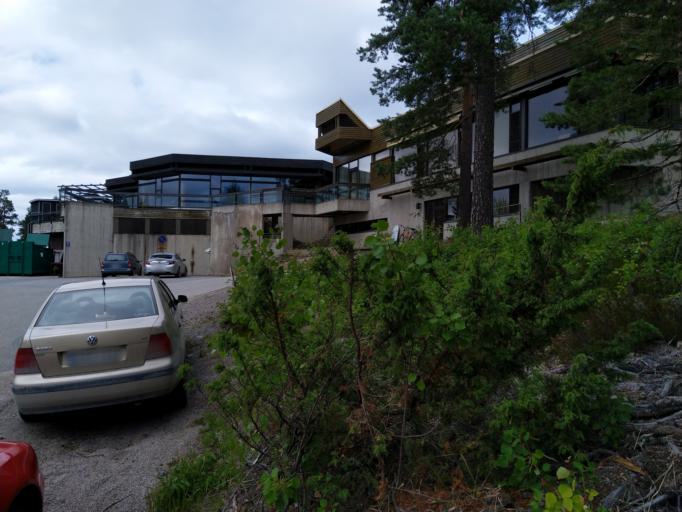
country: FI
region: Southern Ostrobothnia
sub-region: Kuusiokunnat
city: AEhtaeri
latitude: 62.5346
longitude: 24.1825
